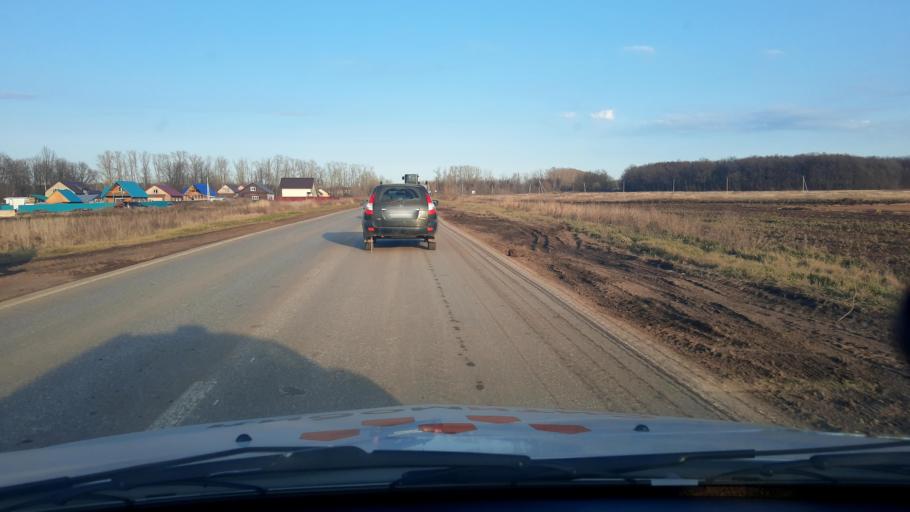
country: RU
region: Bashkortostan
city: Kabakovo
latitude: 54.6966
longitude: 56.1508
